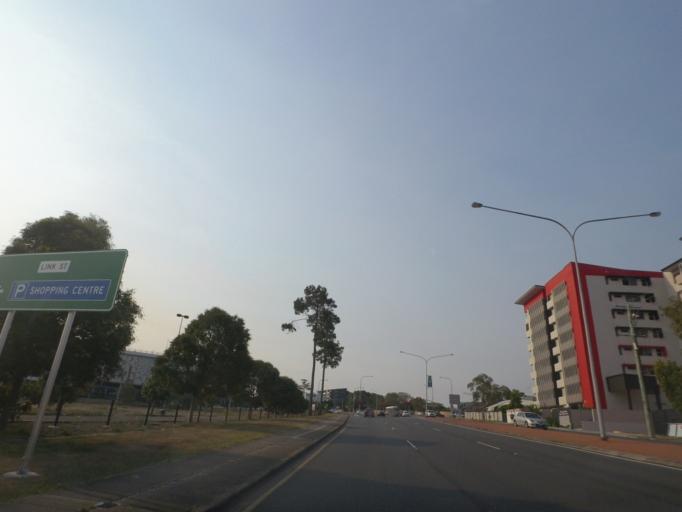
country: AU
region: Queensland
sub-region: Brisbane
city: Upper Mount Gravatt
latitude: -27.5652
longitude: 153.0873
